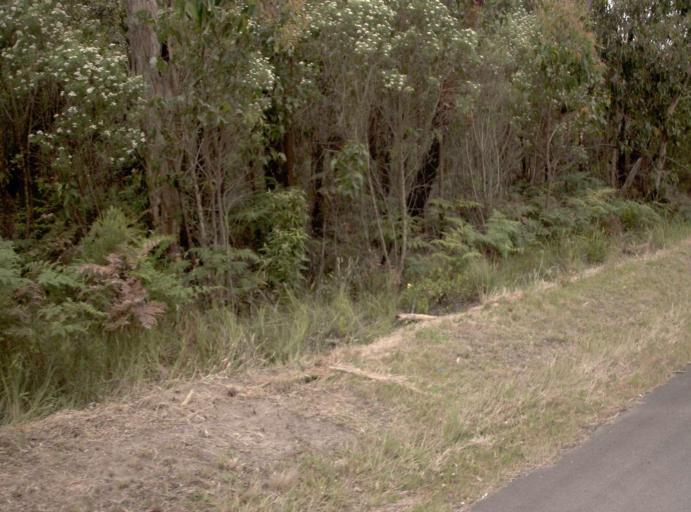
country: AU
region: Victoria
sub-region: Latrobe
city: Moe
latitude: -38.3306
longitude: 146.2522
